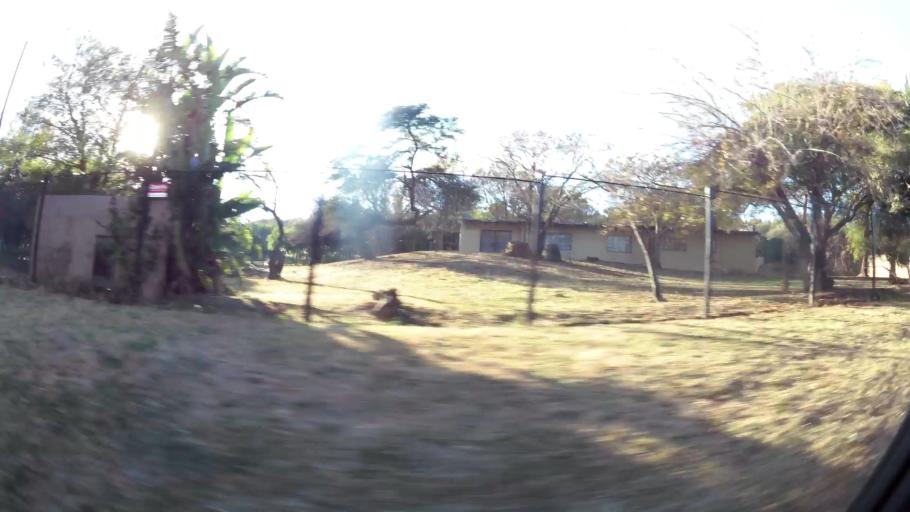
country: ZA
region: Gauteng
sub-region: City of Johannesburg Metropolitan Municipality
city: Midrand
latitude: -26.0308
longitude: 28.0393
